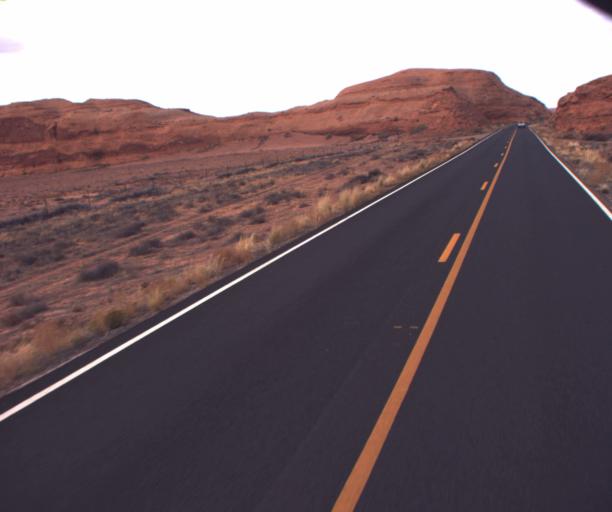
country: US
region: Arizona
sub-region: Apache County
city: Many Farms
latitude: 36.7684
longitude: -109.6572
